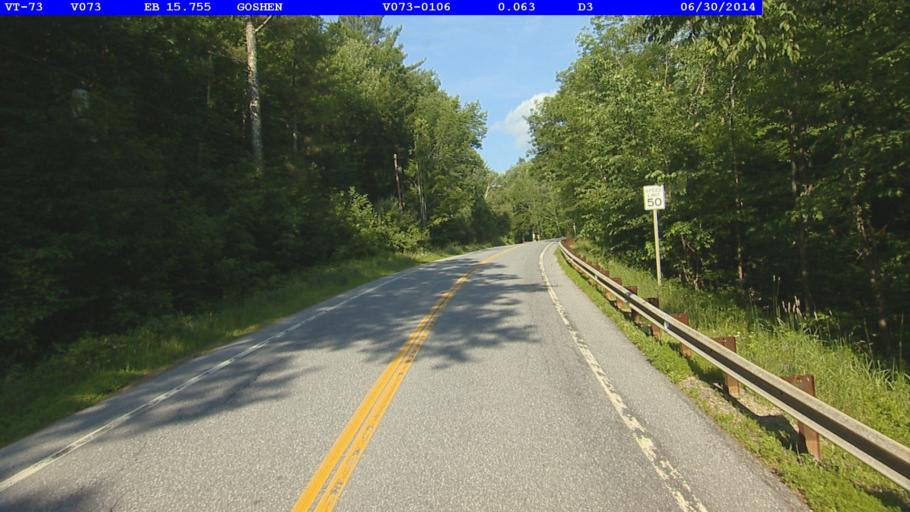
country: US
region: Vermont
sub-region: Rutland County
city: Brandon
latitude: 43.8421
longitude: -73.0285
